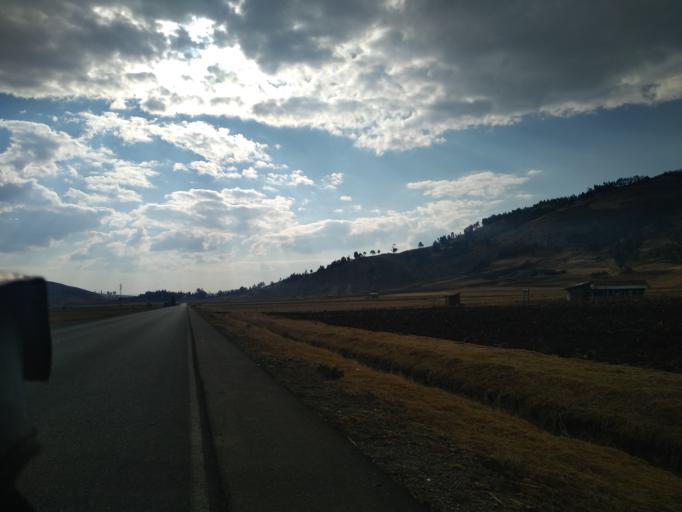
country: PE
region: Cajamarca
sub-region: Provincia de Cajamarca
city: Encanada
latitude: -7.1393
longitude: -78.3791
